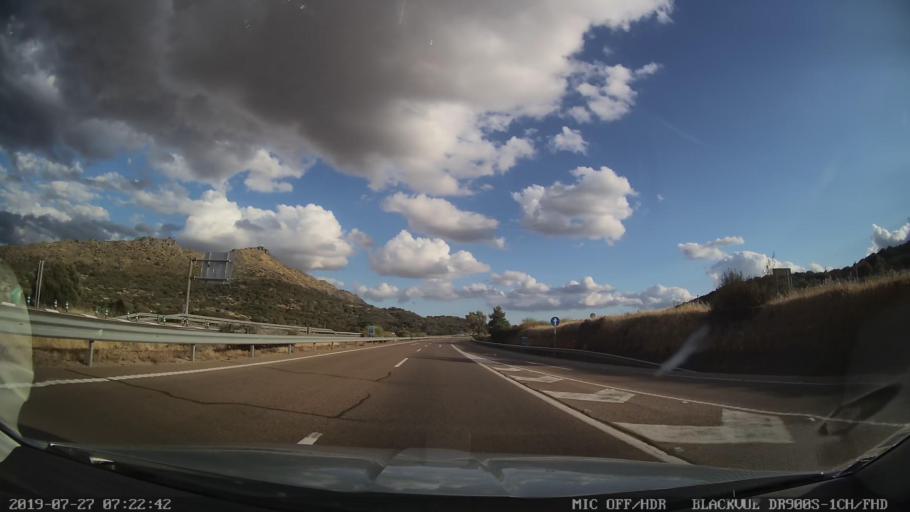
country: ES
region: Extremadura
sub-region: Provincia de Caceres
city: Santa Cruz de la Sierra
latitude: 39.3362
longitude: -5.8567
